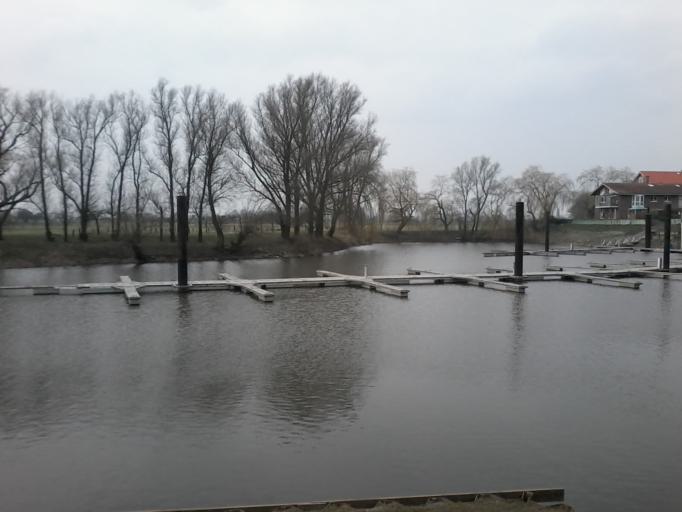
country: DE
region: Lower Saxony
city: Achim
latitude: 52.9963
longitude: 9.0511
